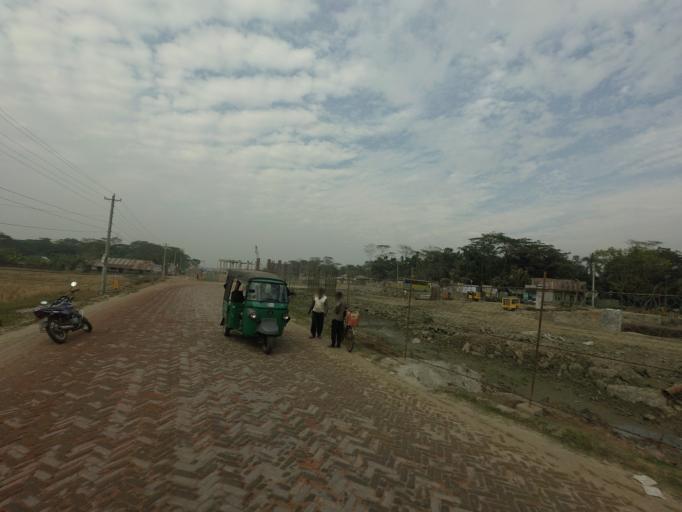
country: BD
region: Barisal
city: Nalchiti
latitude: 22.4592
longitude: 90.3405
